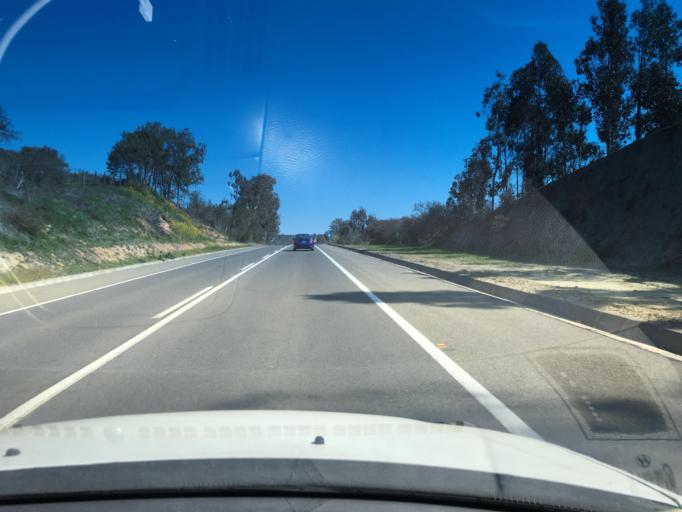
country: CL
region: Valparaiso
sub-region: San Antonio Province
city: El Tabo
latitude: -33.3961
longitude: -71.4904
